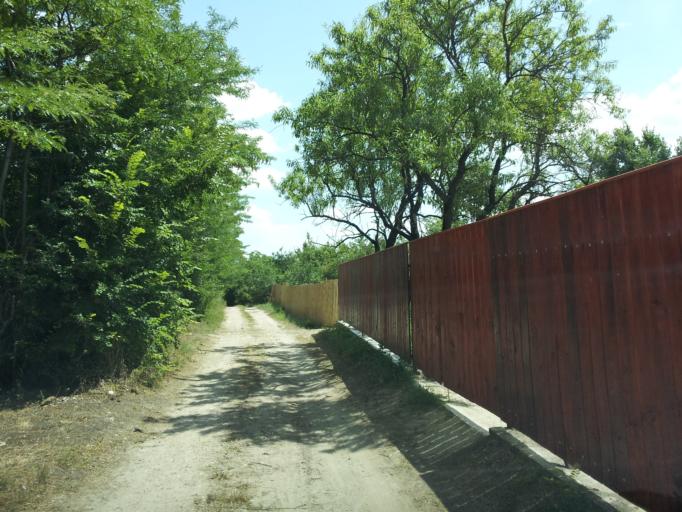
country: HU
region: Veszprem
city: Balatonkenese
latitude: 47.0377
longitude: 18.0924
